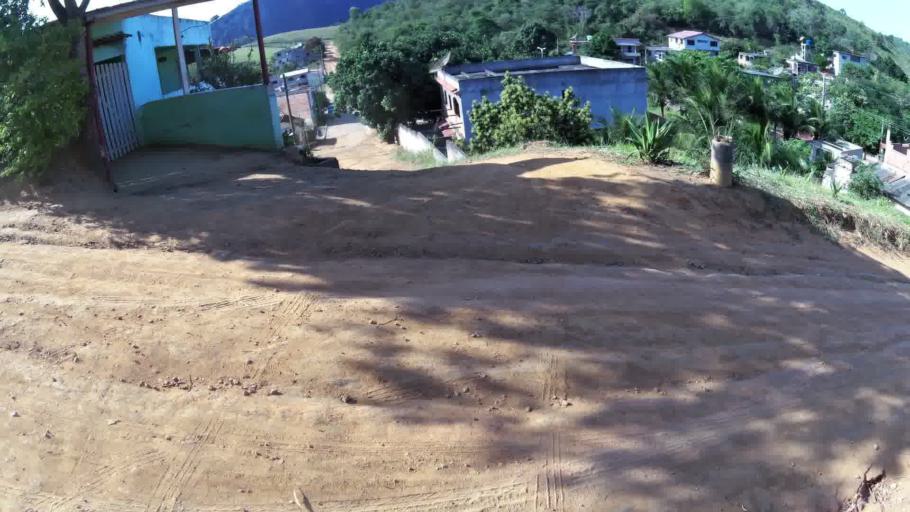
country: BR
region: Espirito Santo
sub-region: Piuma
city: Piuma
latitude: -20.8873
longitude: -40.7712
